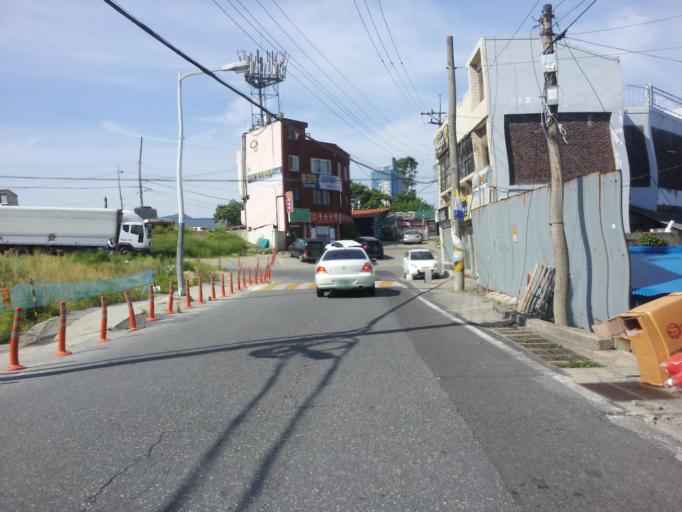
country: KR
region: Daejeon
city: Daejeon
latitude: 36.3362
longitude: 127.4427
